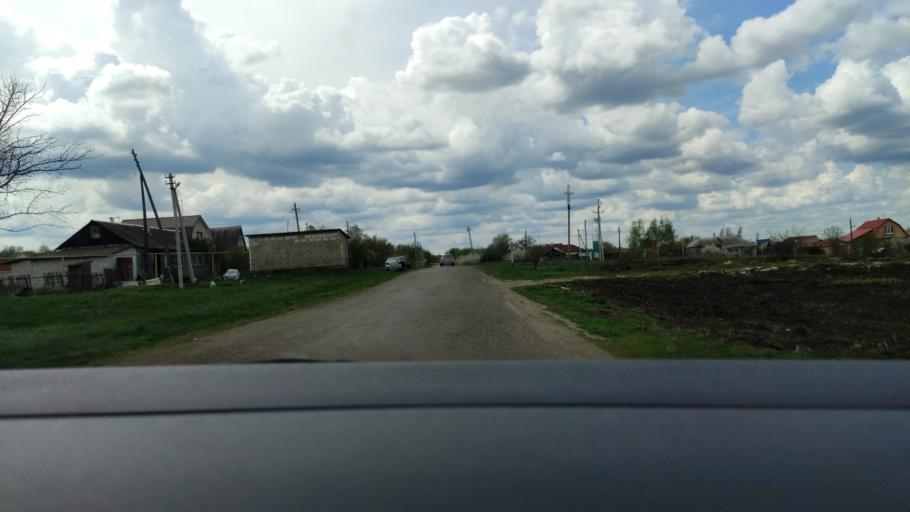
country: RU
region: Voronezj
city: Semiluki
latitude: 51.7795
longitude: 39.0001
